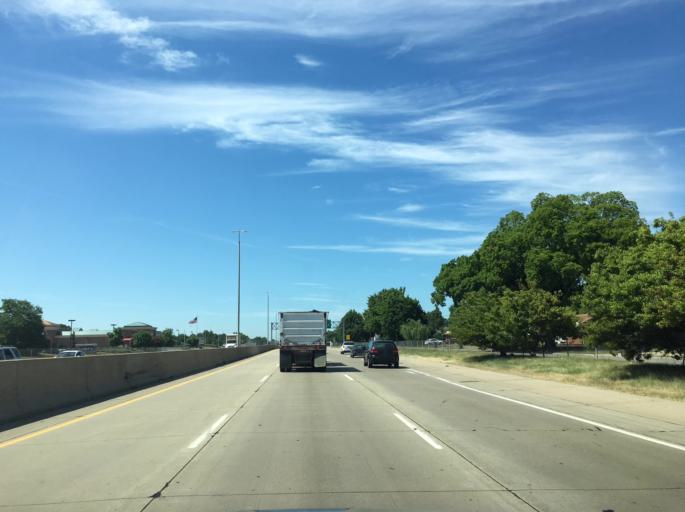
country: US
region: Michigan
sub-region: Wayne County
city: Allen Park
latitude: 42.2817
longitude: -83.2140
